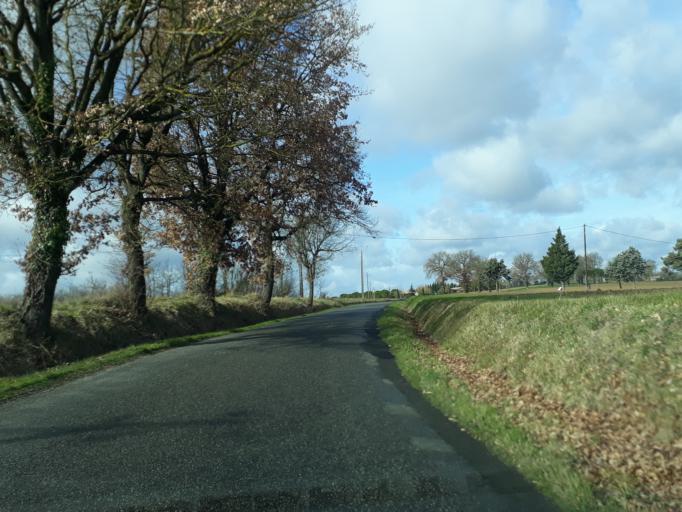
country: FR
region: Midi-Pyrenees
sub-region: Departement du Gers
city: Gimont
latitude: 43.6329
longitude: 1.0086
